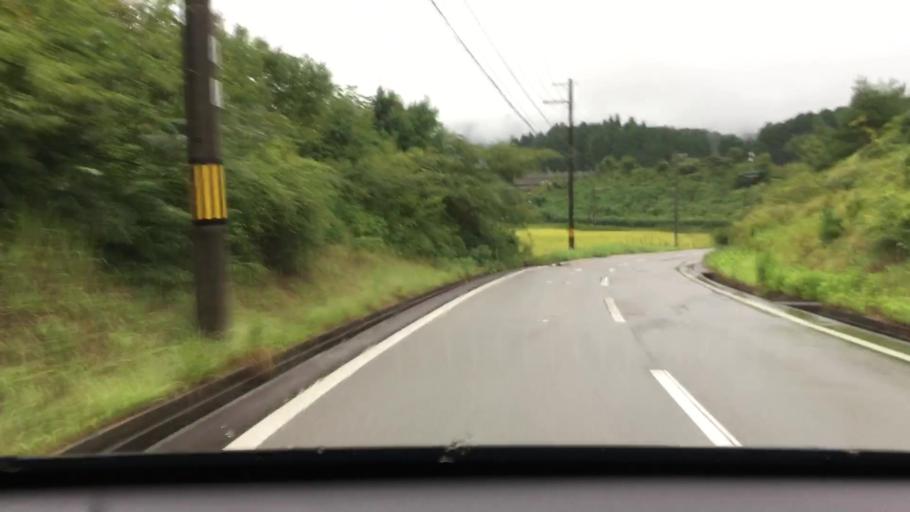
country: JP
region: Hyogo
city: Toyooka
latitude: 35.3117
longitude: 134.8715
